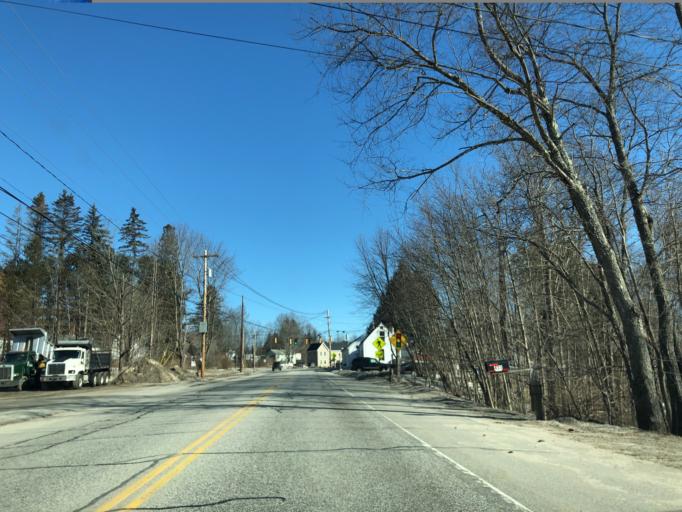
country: US
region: Maine
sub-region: Cumberland County
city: South Windham
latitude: 43.7884
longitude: -70.4094
